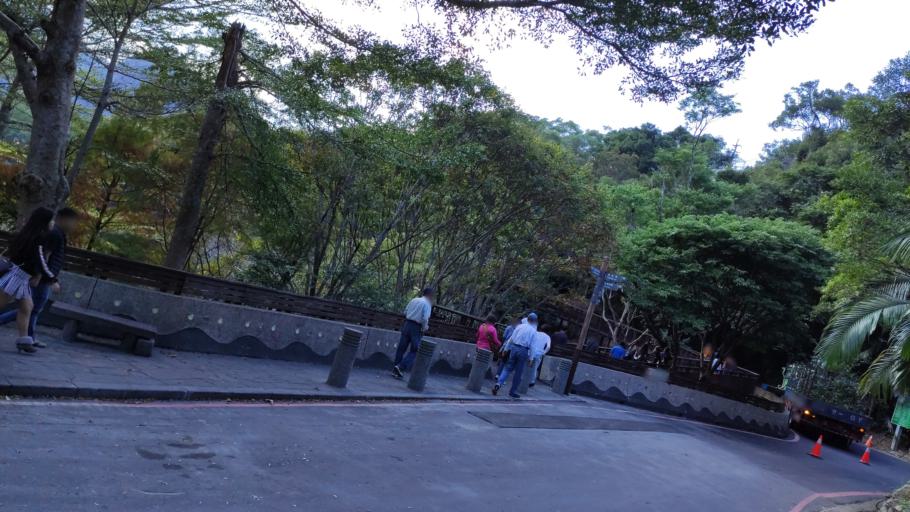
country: TW
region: Taiwan
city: Daxi
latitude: 24.7909
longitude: 121.3776
